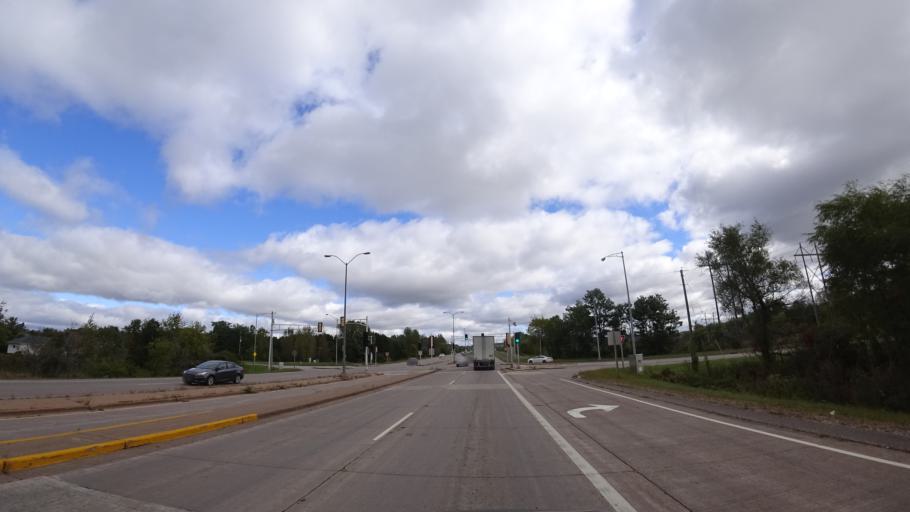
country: US
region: Wisconsin
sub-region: Eau Claire County
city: Eau Claire
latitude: 44.8411
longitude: -91.5084
